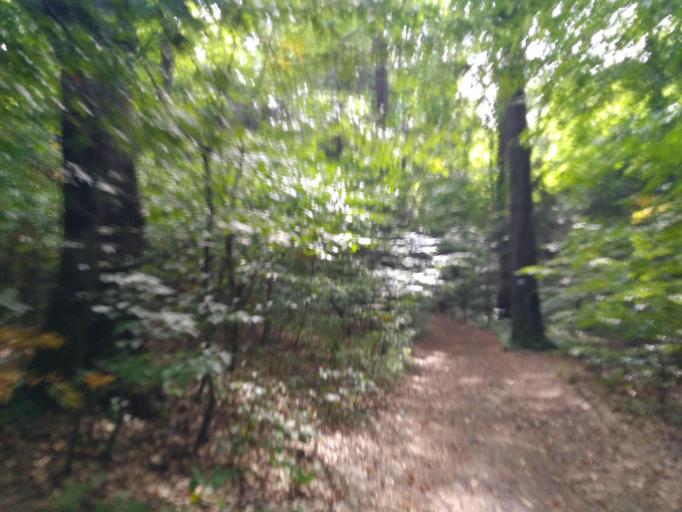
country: PL
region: Subcarpathian Voivodeship
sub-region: Powiat strzyzowski
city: Frysztak
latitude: 49.8870
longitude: 21.5632
